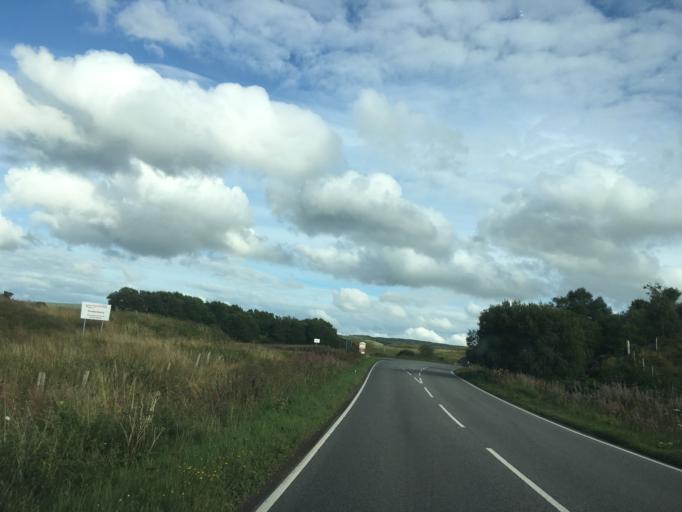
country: GB
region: Scotland
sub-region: Argyll and Bute
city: Oban
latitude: 56.3931
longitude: -5.4635
